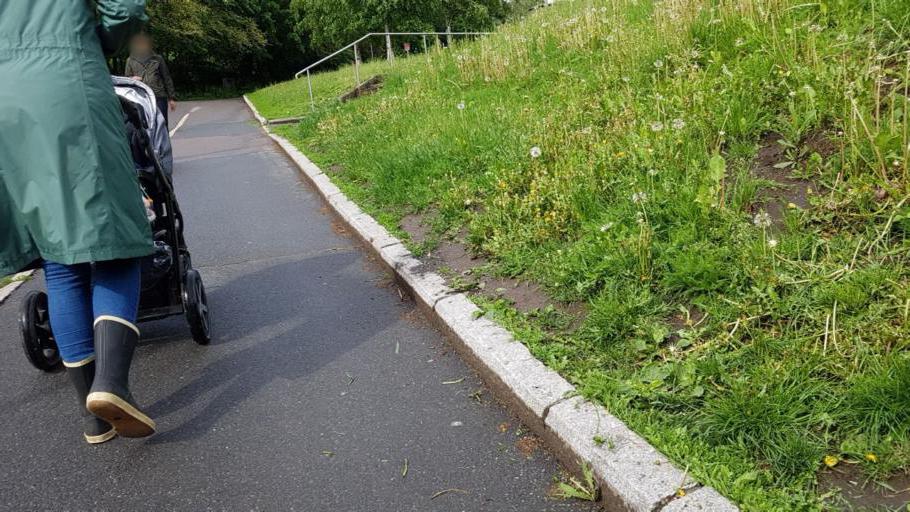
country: NO
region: Oslo
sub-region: Oslo
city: Oslo
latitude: 59.9310
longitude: 10.7716
